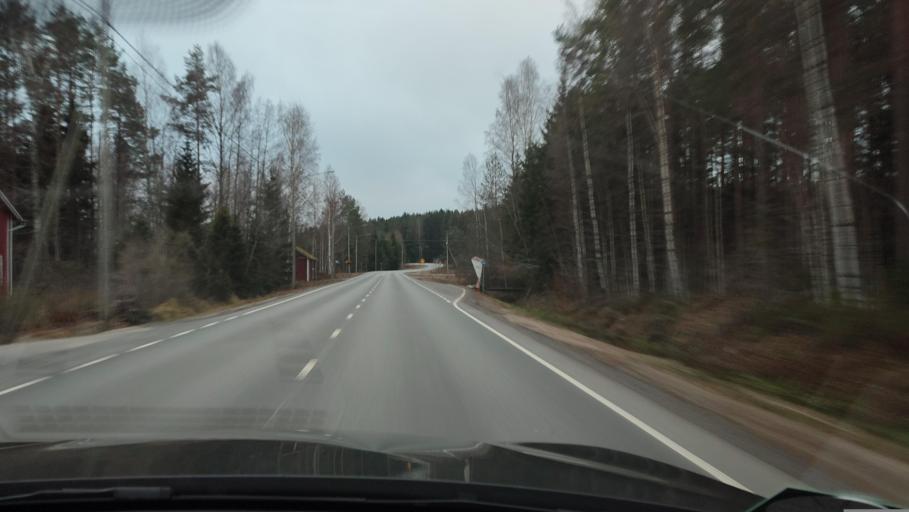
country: FI
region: Southern Ostrobothnia
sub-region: Suupohja
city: Karijoki
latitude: 62.3028
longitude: 21.6892
